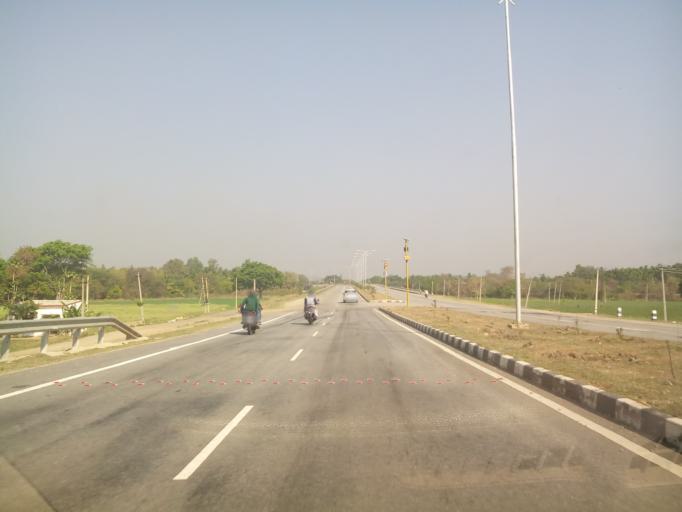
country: IN
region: Karnataka
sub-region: Tumkur
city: Kunigal
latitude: 13.0015
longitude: 77.0185
